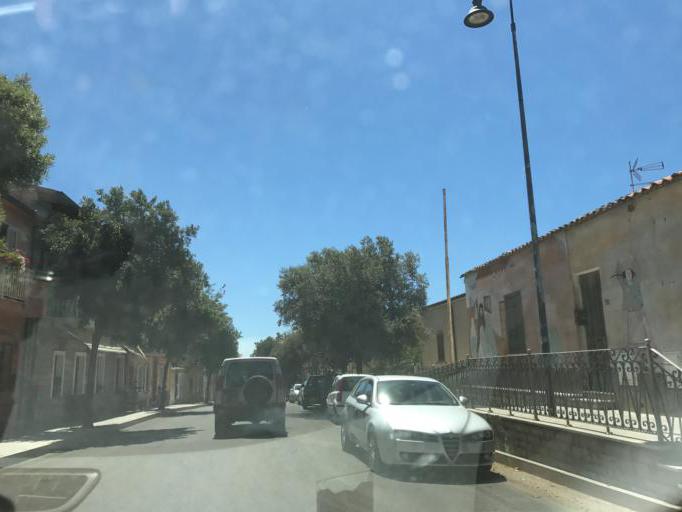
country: IT
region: Sardinia
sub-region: Provincia di Olbia-Tempio
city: Telti
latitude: 40.8755
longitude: 9.3533
